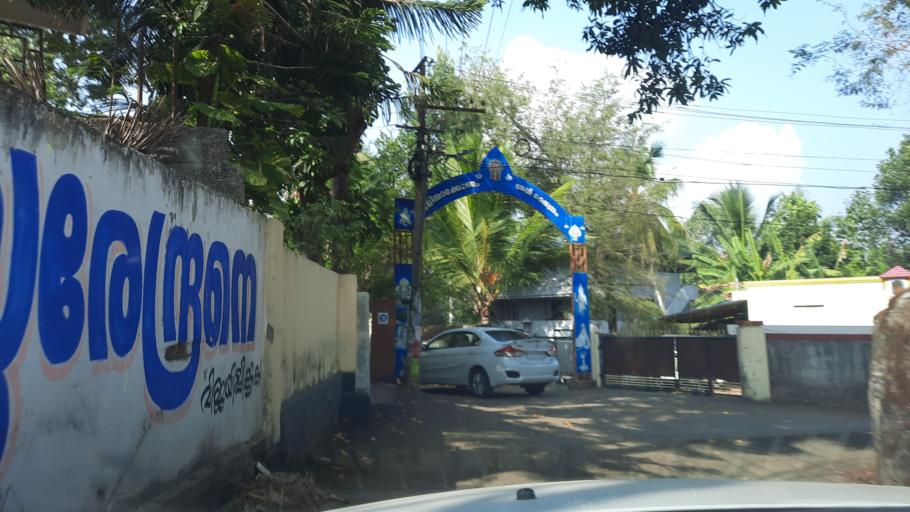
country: IN
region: Kerala
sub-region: Thiruvananthapuram
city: Thiruvananthapuram
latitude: 8.5606
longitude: 76.9231
